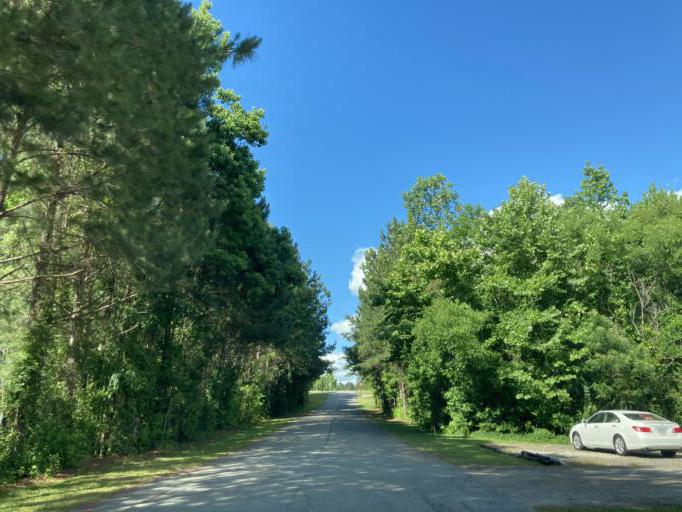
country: US
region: Georgia
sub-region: Jones County
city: Gray
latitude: 32.9951
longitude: -83.5478
